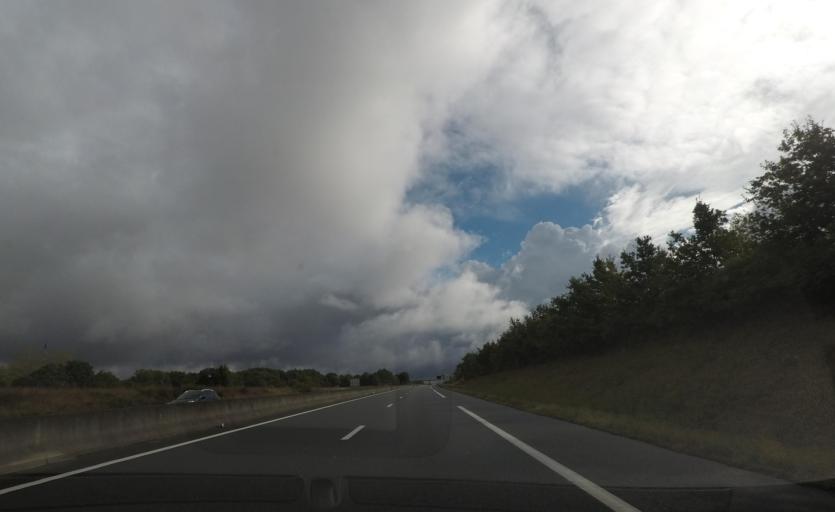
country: FR
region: Pays de la Loire
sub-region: Departement de la Vendee
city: La Roche-sur-Yon
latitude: 46.6560
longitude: -1.3809
